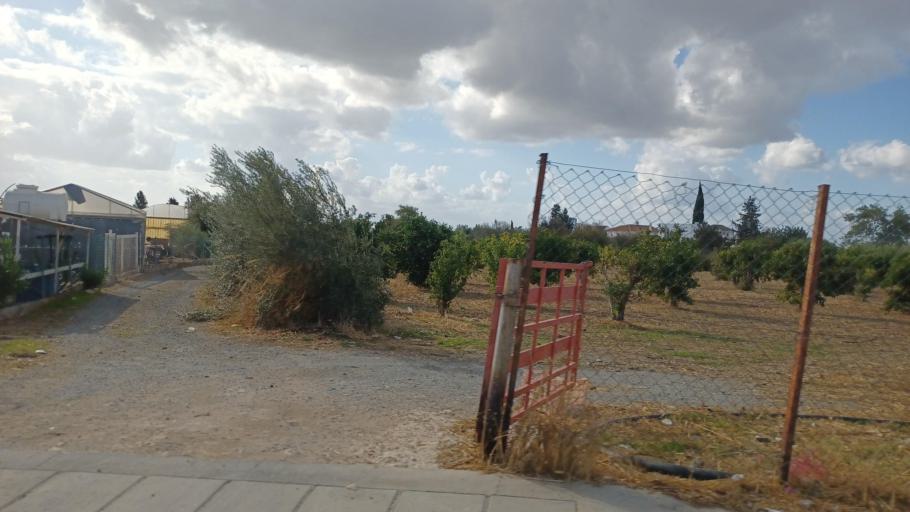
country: CY
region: Limassol
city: Pano Polemidia
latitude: 34.6915
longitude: 33.0037
